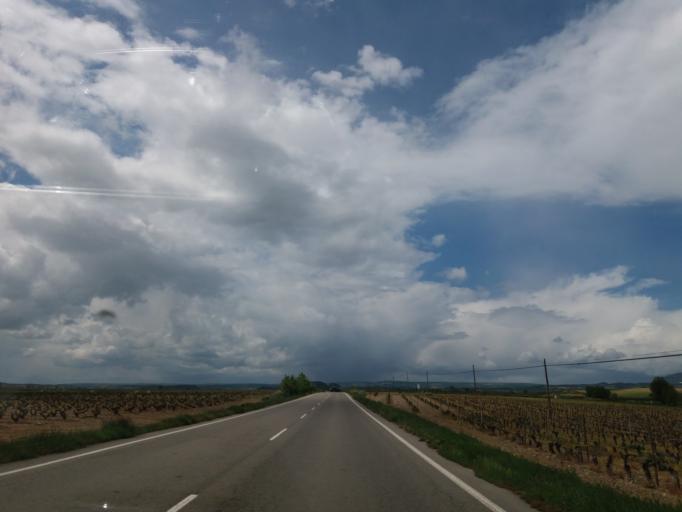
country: ES
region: La Rioja
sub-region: Provincia de La Rioja
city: Cihuri
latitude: 42.5741
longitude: -2.9254
